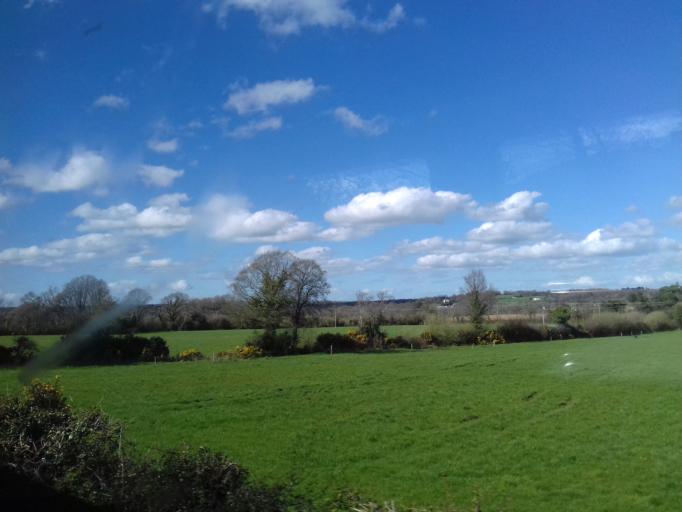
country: IE
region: Munster
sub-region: County Cork
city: Kanturk
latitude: 52.1242
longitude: -8.8155
